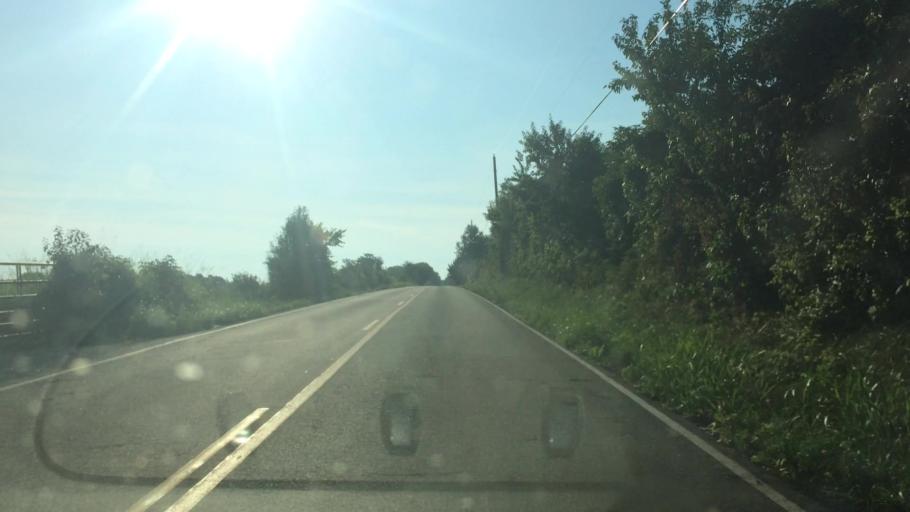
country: US
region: Missouri
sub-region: Greene County
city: Strafford
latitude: 37.2560
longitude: -93.1853
